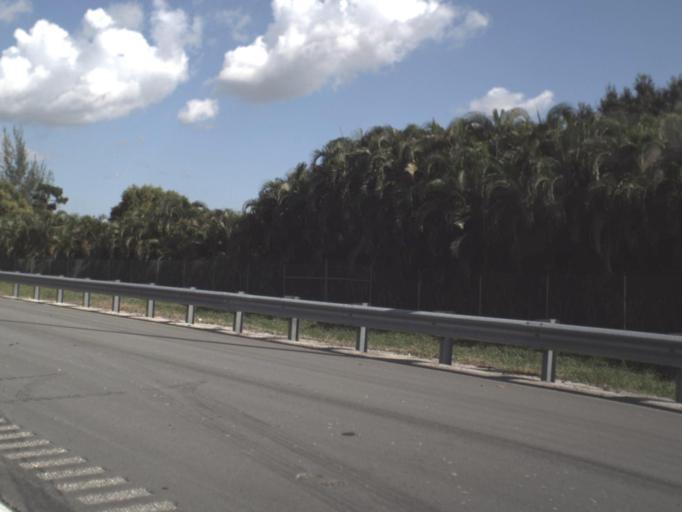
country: US
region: Florida
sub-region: Palm Beach County
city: Villages of Oriole
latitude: 26.4811
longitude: -80.1726
